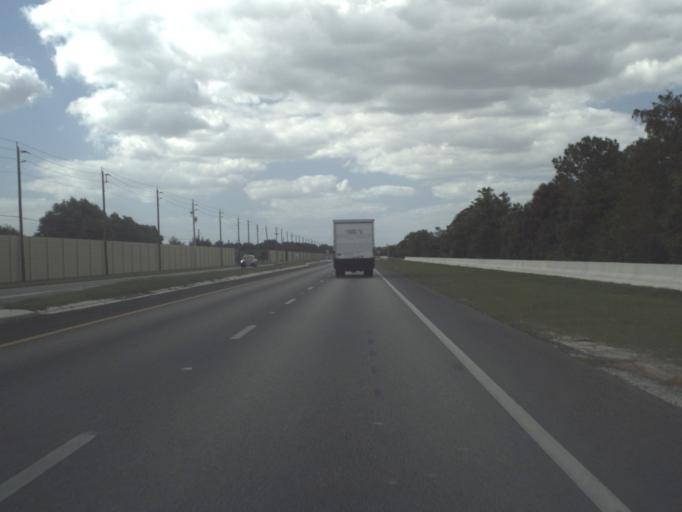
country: US
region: Florida
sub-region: Collier County
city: Lely Resort
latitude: 26.0362
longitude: -81.6569
